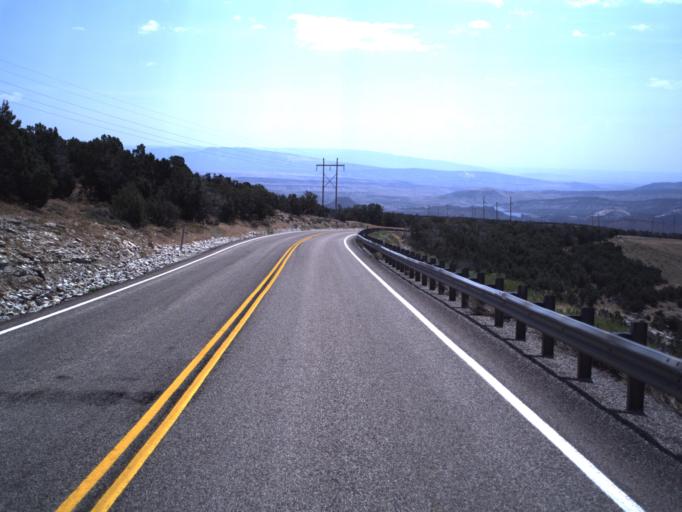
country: US
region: Utah
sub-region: Uintah County
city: Vernal
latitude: 40.6393
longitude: -109.4817
